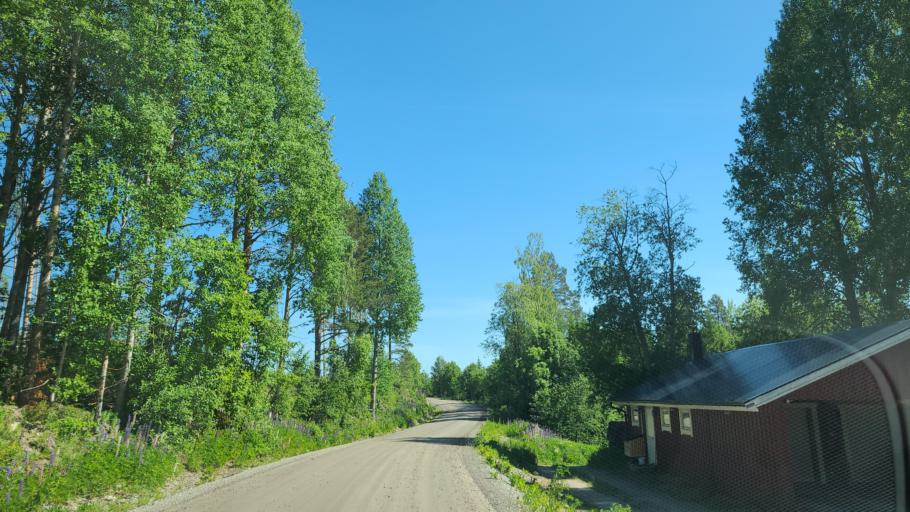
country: SE
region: Vaesterbotten
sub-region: Bjurholms Kommun
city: Bjurholm
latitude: 63.6743
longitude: 19.0268
